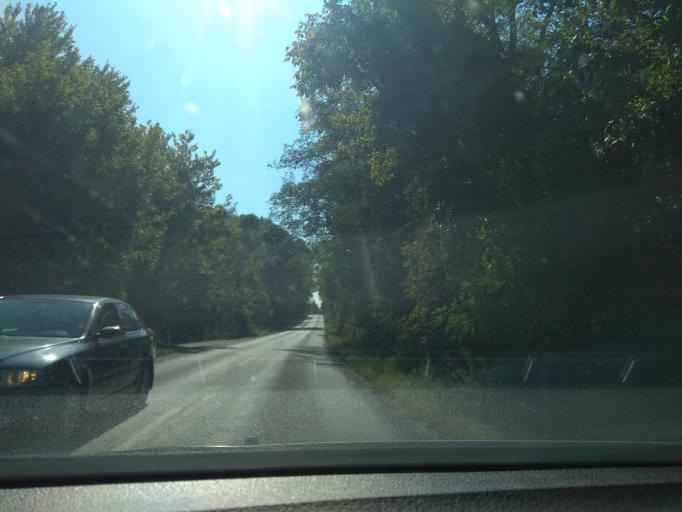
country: HU
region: Borsod-Abauj-Zemplen
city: Harsany
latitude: 48.0251
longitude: 20.7655
